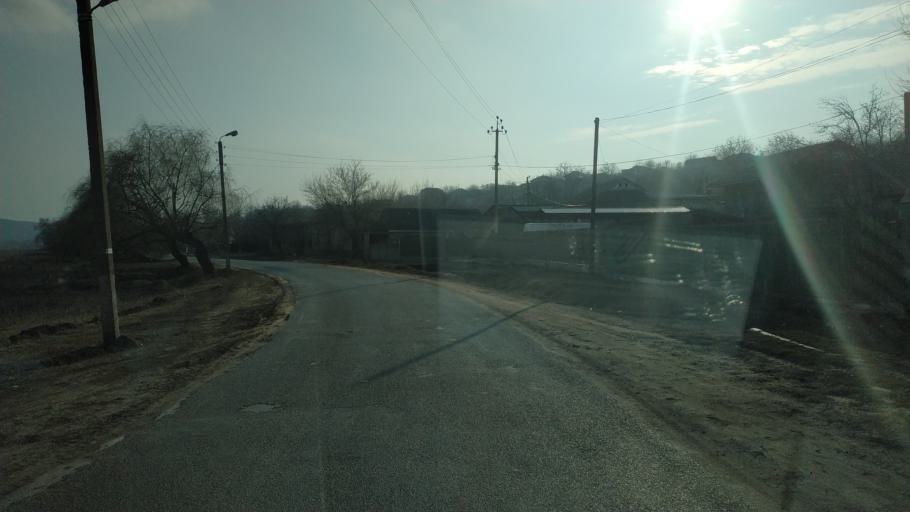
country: MD
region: Hincesti
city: Dancu
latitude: 46.7757
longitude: 28.3463
